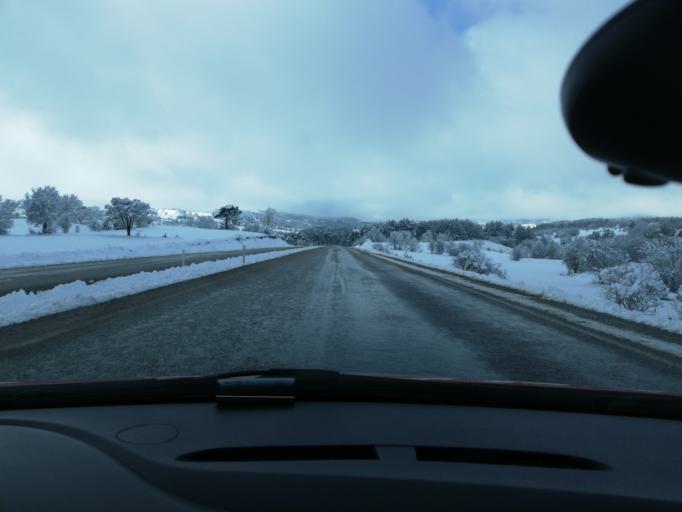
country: TR
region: Kastamonu
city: Ihsangazi
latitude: 41.3149
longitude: 33.6005
